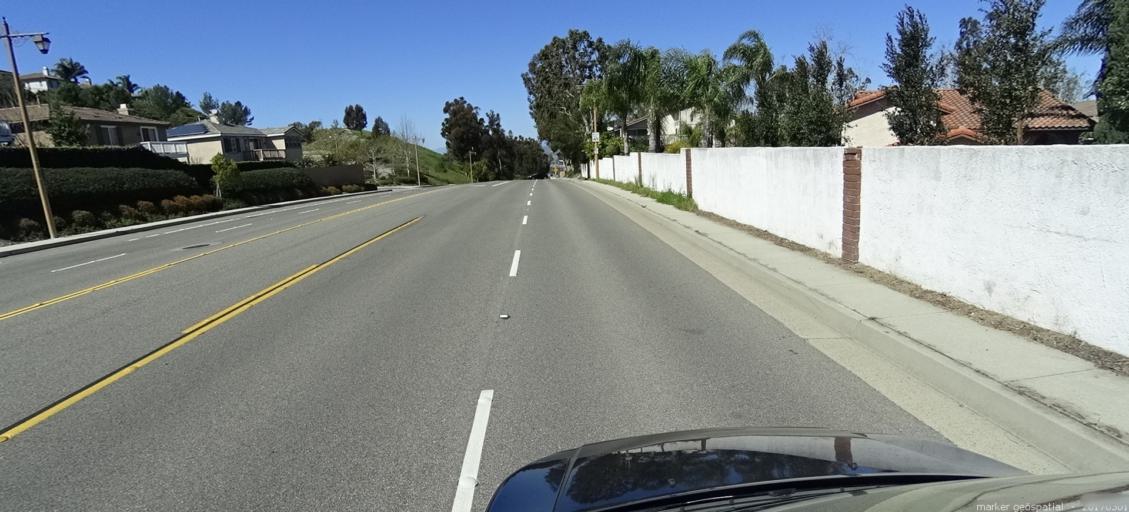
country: US
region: California
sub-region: Orange County
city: Villa Park
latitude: 33.8327
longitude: -117.7619
